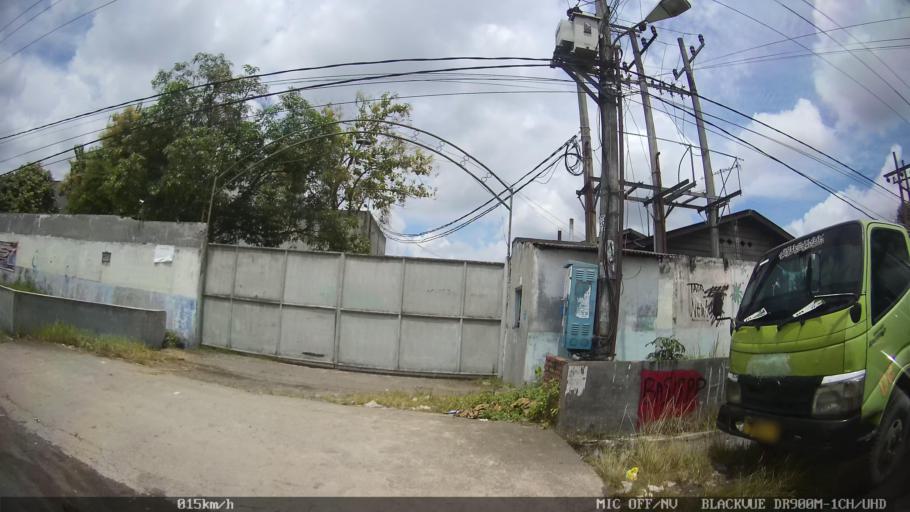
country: ID
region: North Sumatra
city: Medan
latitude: 3.6182
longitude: 98.7482
